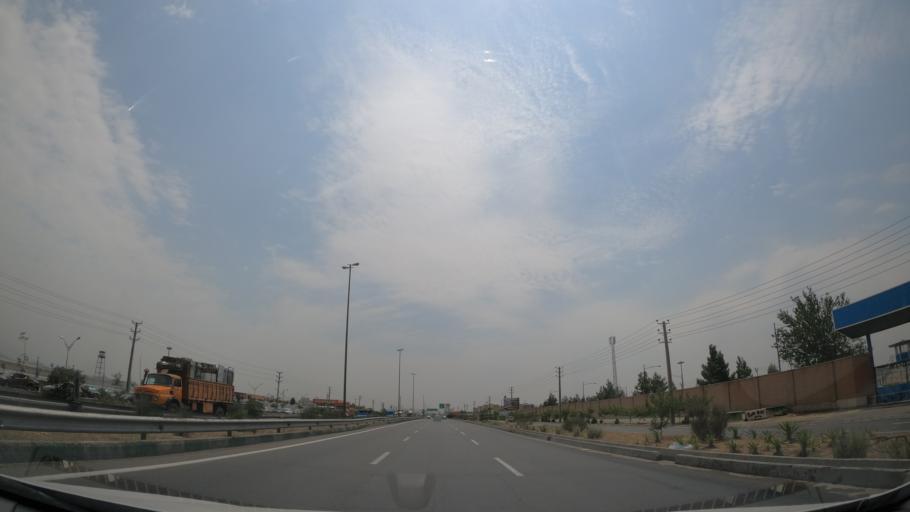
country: IR
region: Tehran
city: Shahr-e Qods
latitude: 35.6986
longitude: 51.1951
